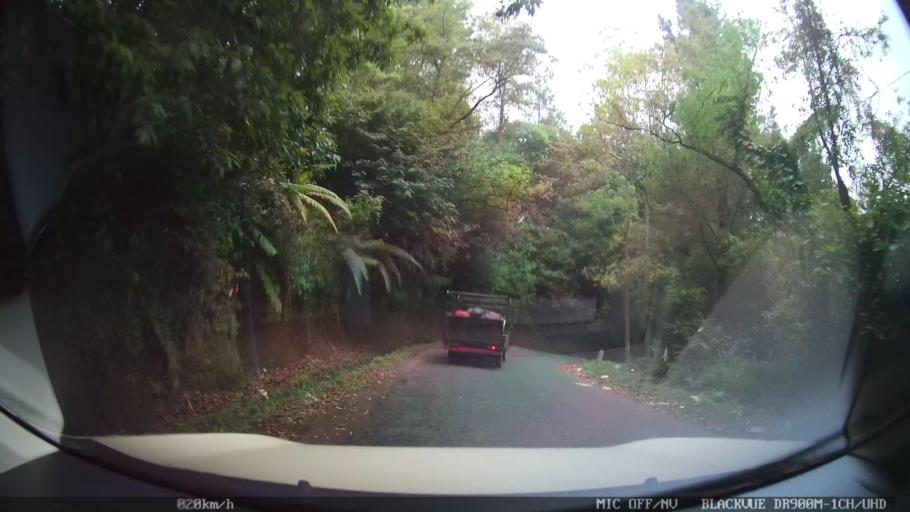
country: ID
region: Bali
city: Banjar Kedisan
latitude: -8.2608
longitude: 115.3351
